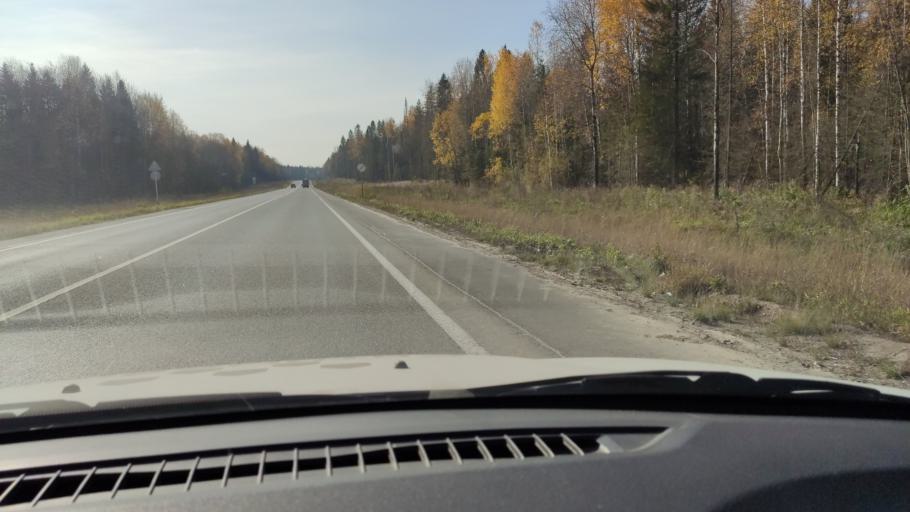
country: RU
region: Perm
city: Novyye Lyady
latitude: 58.0411
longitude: 56.5402
